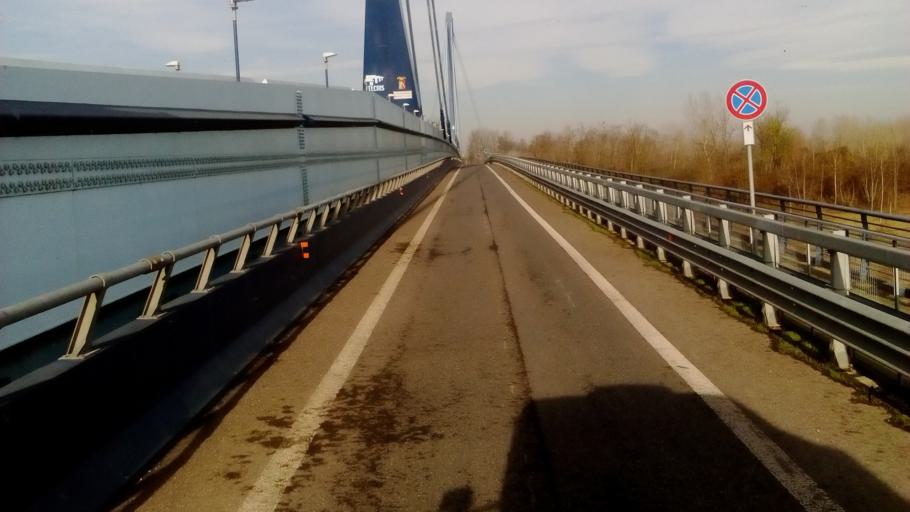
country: IT
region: Lombardy
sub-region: Provincia di Cremona
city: Gombito
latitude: 45.2526
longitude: 9.7005
